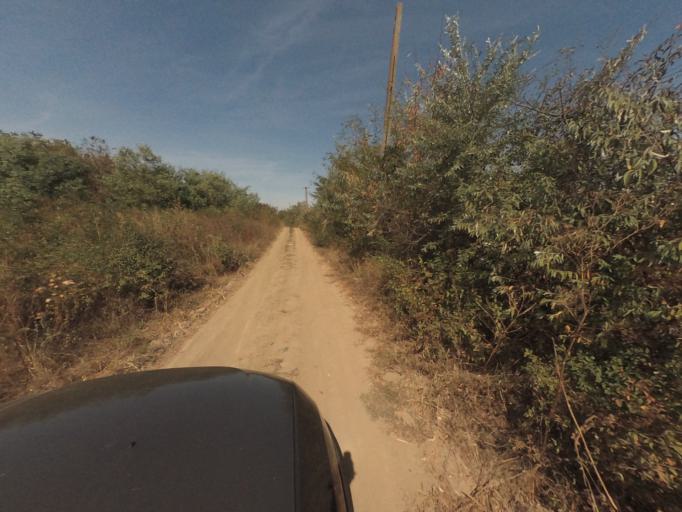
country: RO
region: Vaslui
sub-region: Comuna Costesti
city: Costesti
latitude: 46.5176
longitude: 27.7419
